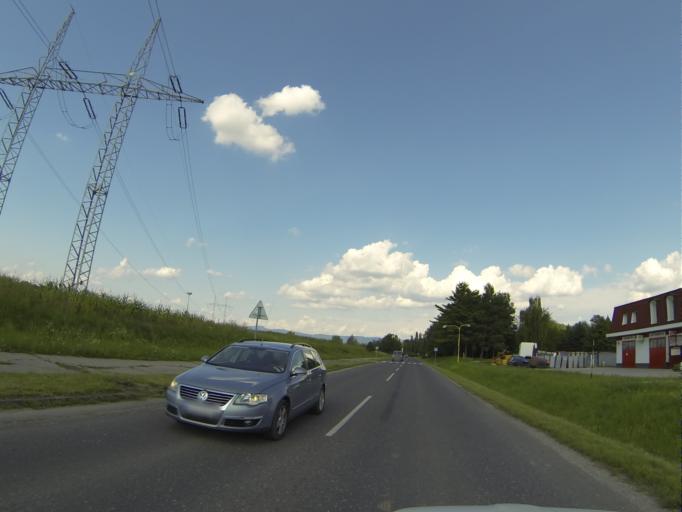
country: SK
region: Nitriansky
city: Bojnice
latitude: 48.7765
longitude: 18.5909
